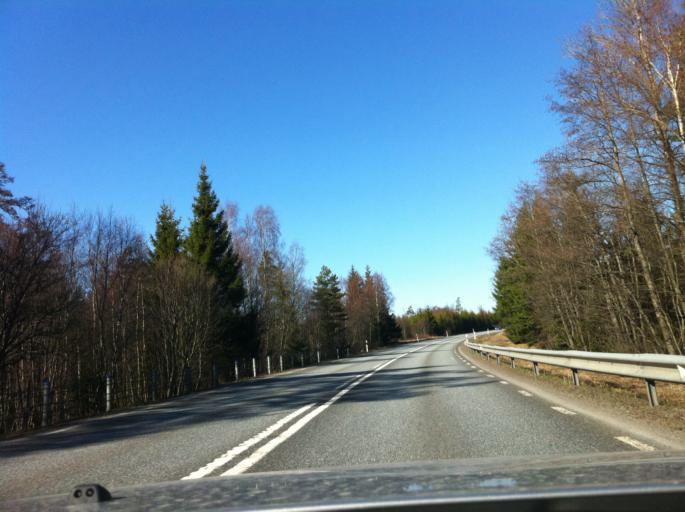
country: SE
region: Joenkoeping
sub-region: Mullsjo Kommun
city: Mullsjoe
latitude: 58.0166
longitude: 13.8278
